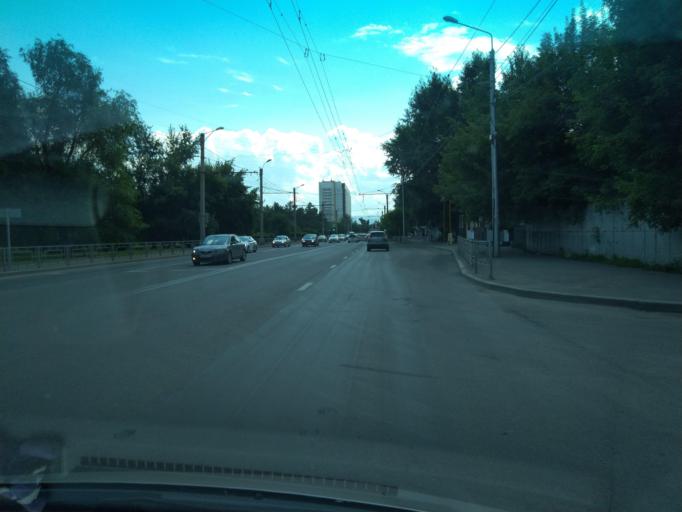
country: RU
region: Krasnoyarskiy
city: Solnechnyy
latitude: 56.0456
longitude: 92.9413
